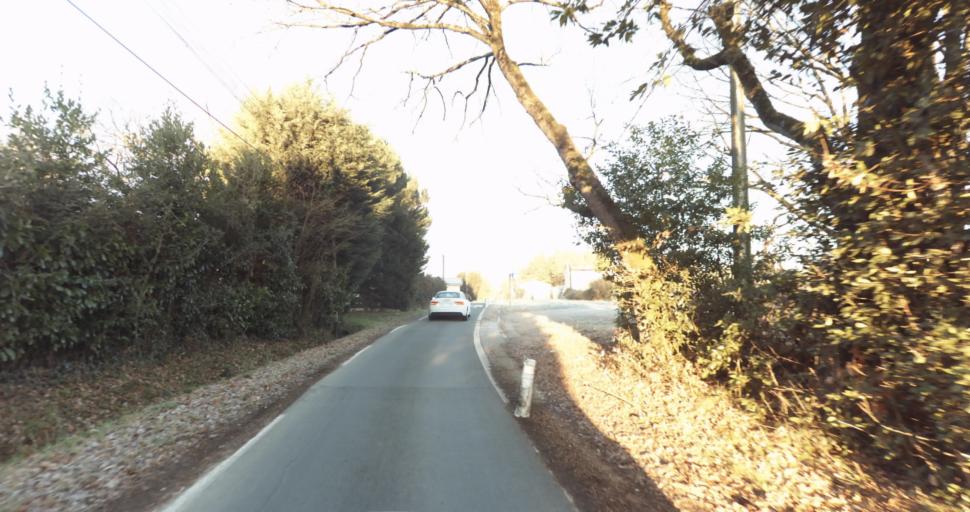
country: FR
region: Aquitaine
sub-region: Departement de la Gironde
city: Ambares-et-Lagrave
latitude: 44.9172
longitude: -0.4966
